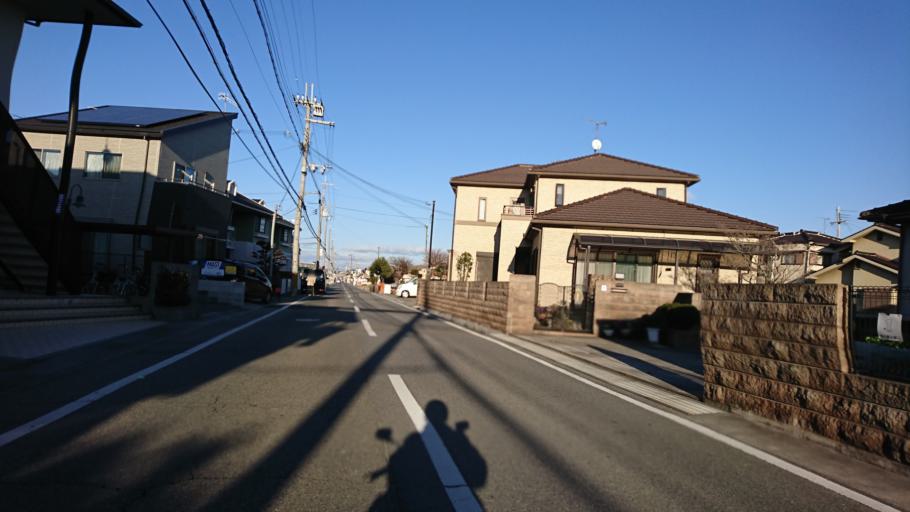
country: JP
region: Hyogo
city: Kakogawacho-honmachi
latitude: 34.7560
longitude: 134.8151
